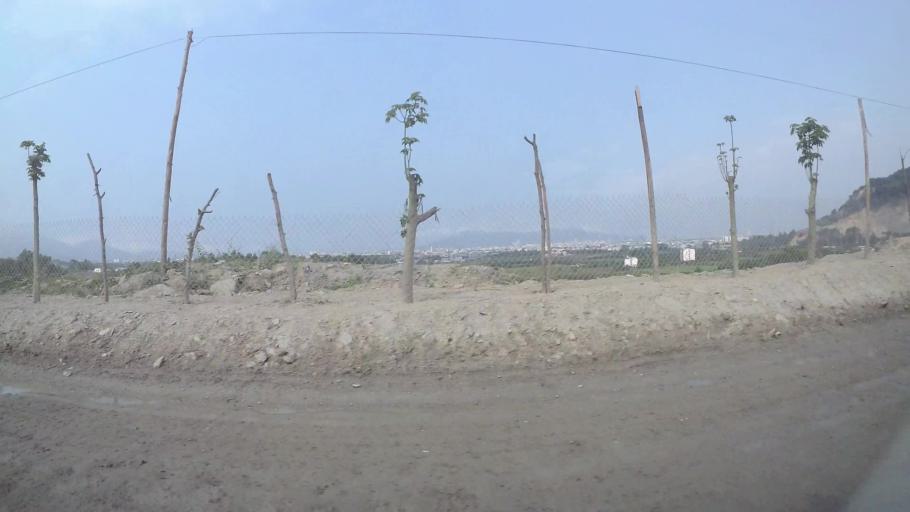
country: VN
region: Da Nang
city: Lien Chieu
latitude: 16.0407
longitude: 108.1510
